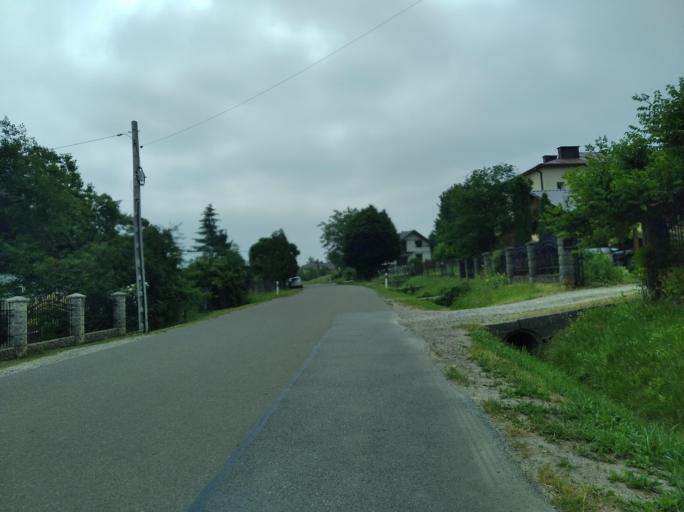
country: PL
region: Subcarpathian Voivodeship
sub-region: Powiat sanocki
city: Besko
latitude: 49.5935
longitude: 21.9367
